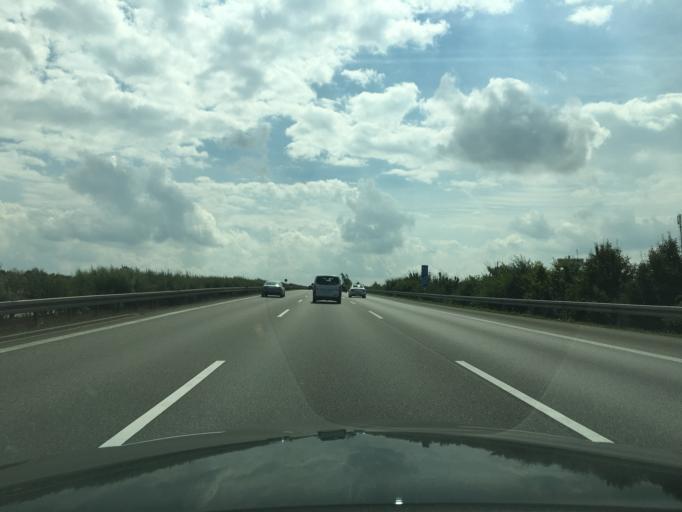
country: DE
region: Thuringia
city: Walpernhain
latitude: 51.0443
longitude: 11.9413
